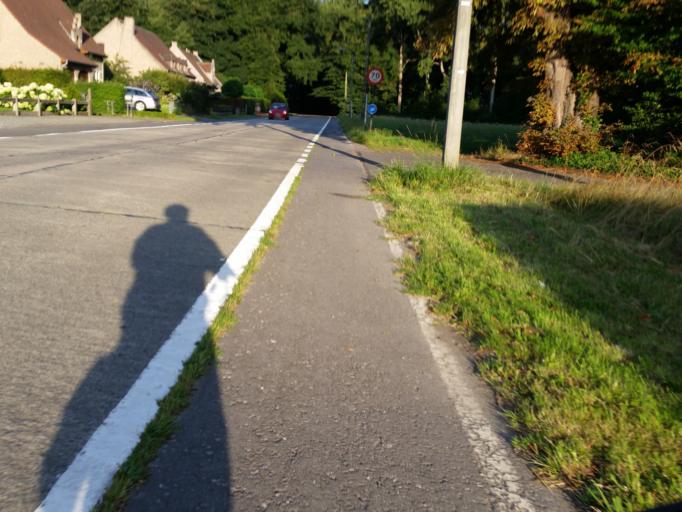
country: BE
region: Flanders
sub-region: Provincie Vlaams-Brabant
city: Zemst
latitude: 50.9795
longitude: 4.4455
